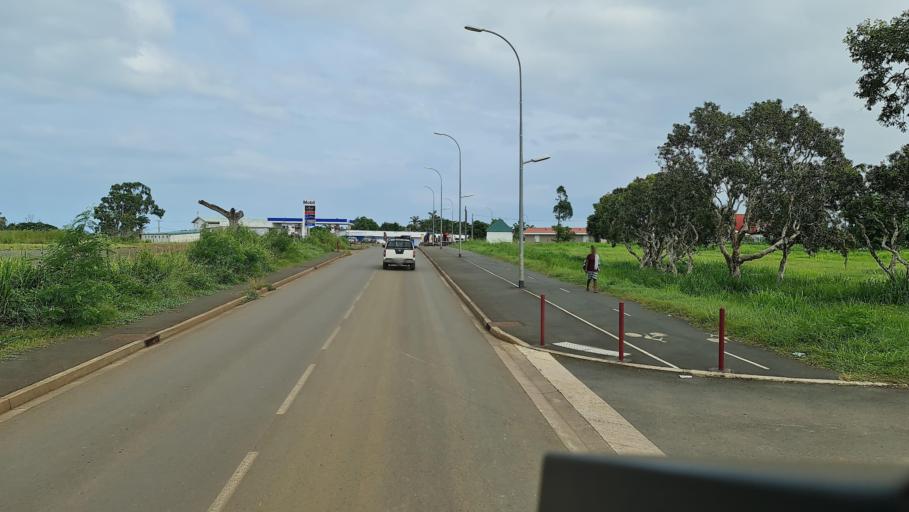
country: NC
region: North Province
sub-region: Koumac
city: Koumac
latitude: -20.5621
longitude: 164.2832
